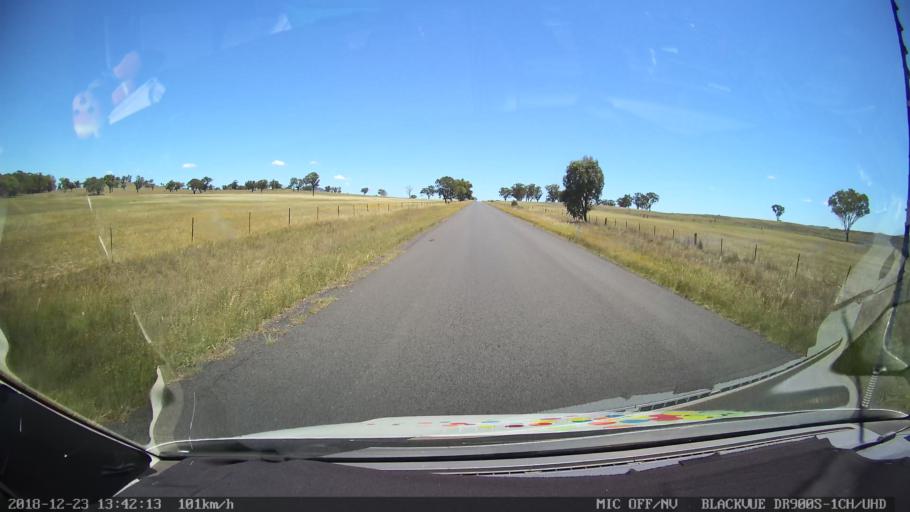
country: AU
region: New South Wales
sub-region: Armidale Dumaresq
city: Armidale
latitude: -30.4745
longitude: 151.1651
